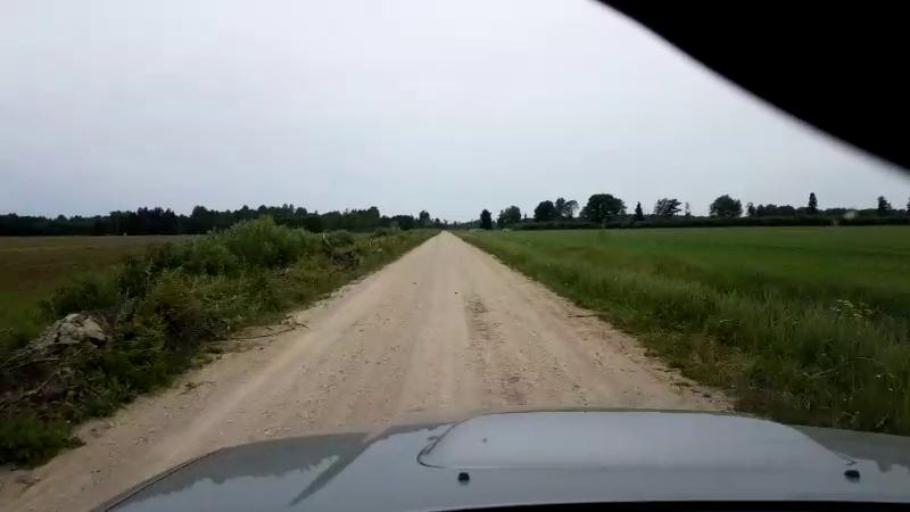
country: EE
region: Paernumaa
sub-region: Halinga vald
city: Parnu-Jaagupi
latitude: 58.5457
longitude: 24.6154
